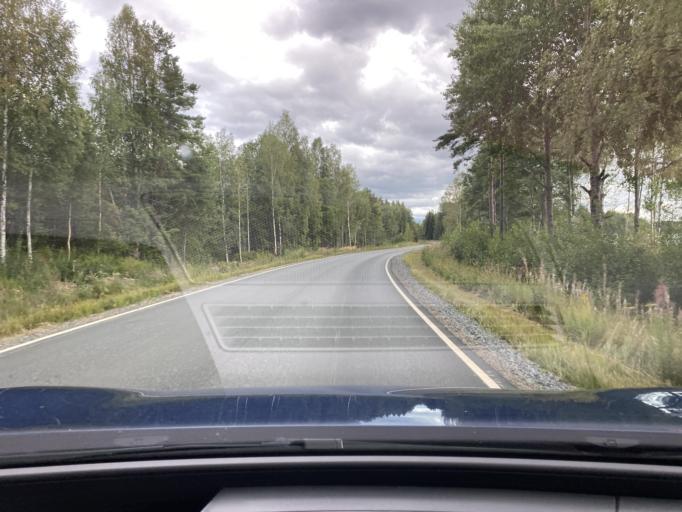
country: FI
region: Pirkanmaa
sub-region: Lounais-Pirkanmaa
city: Vammala
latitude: 61.3017
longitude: 22.9549
